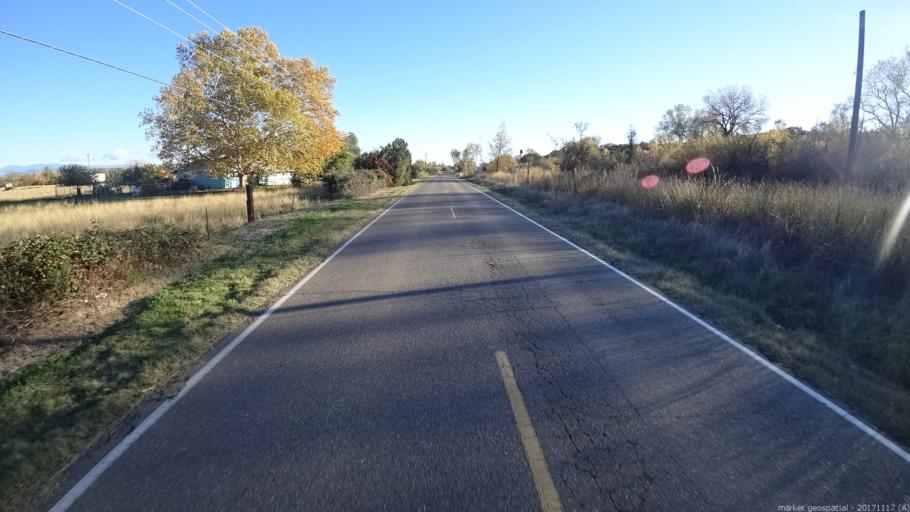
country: US
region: California
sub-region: Shasta County
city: Cottonwood
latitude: 40.4113
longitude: -122.2466
